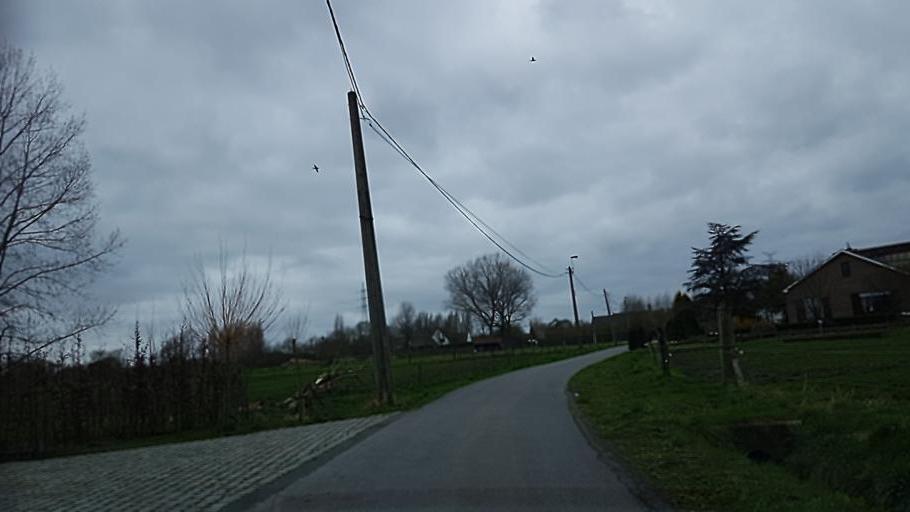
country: BE
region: Flanders
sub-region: Provincie Antwerpen
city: Duffel
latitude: 51.1104
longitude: 4.5123
